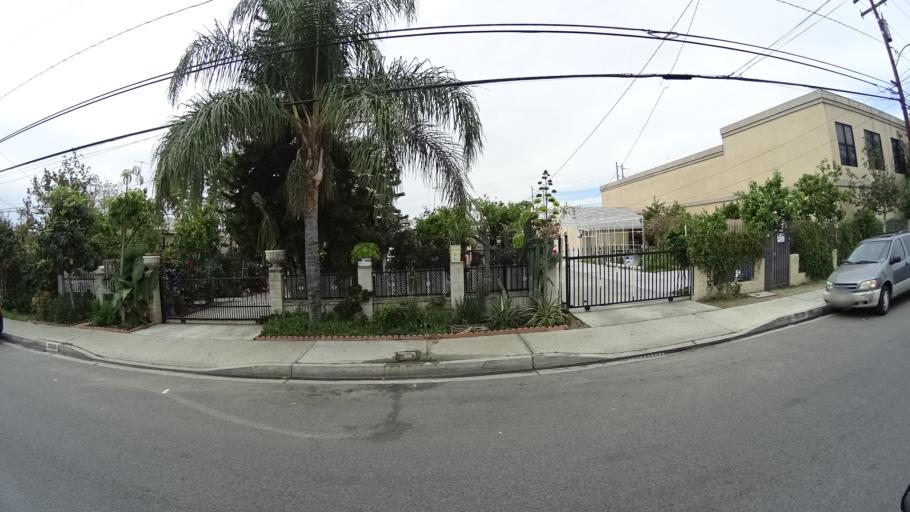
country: US
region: California
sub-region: Los Angeles County
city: West Puente Valley
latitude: 34.0676
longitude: -117.9925
